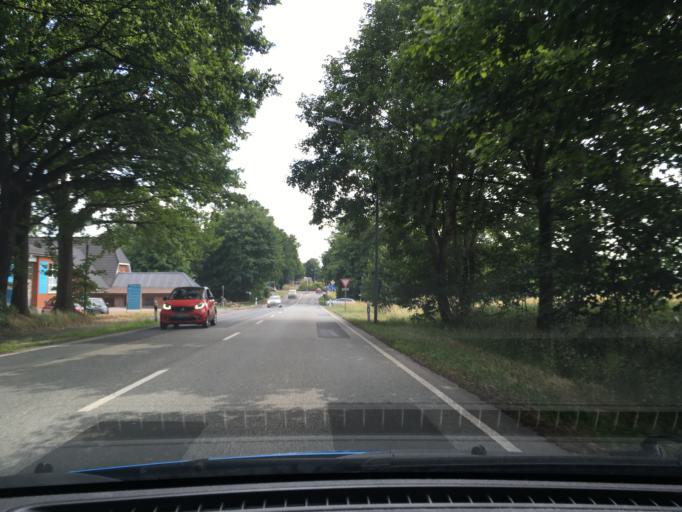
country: DE
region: Lower Saxony
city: Kakenstorf
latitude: 53.3115
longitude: 9.8039
